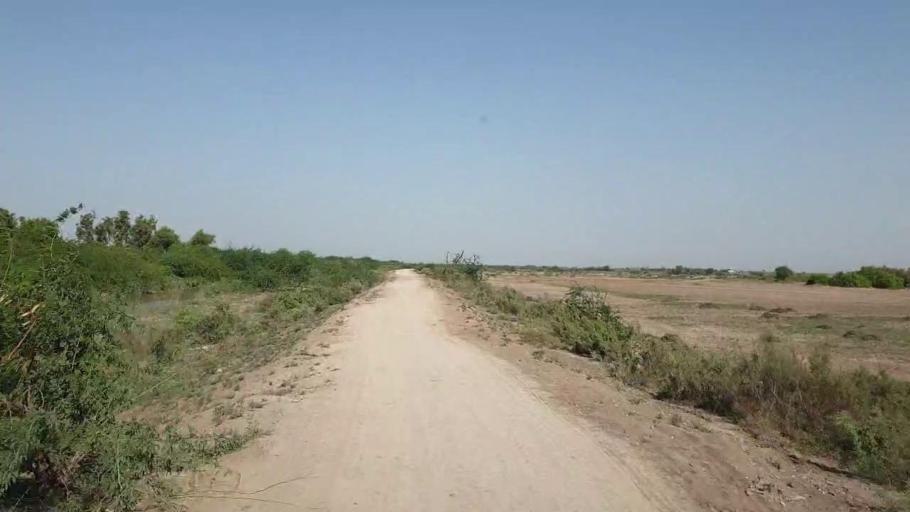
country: PK
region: Sindh
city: Tando Bago
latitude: 24.6499
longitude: 69.0712
